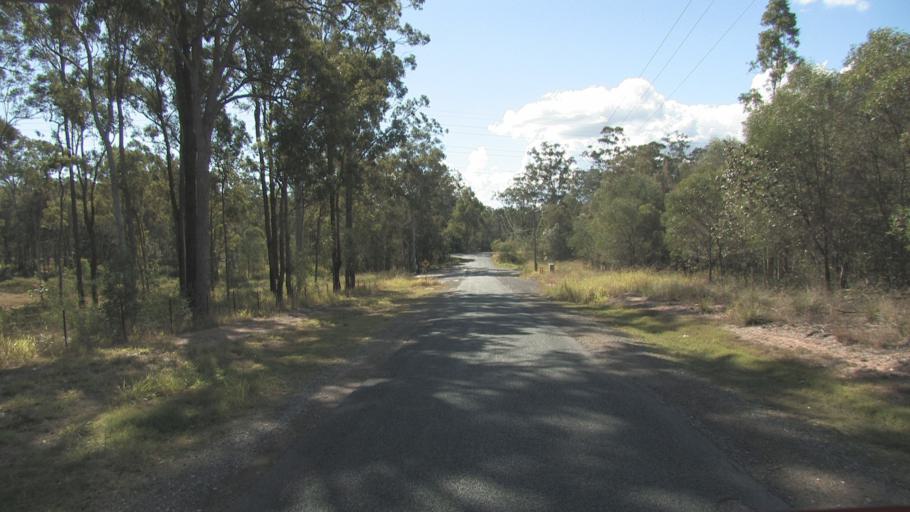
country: AU
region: Queensland
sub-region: Logan
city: Chambers Flat
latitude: -27.8047
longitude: 153.0829
